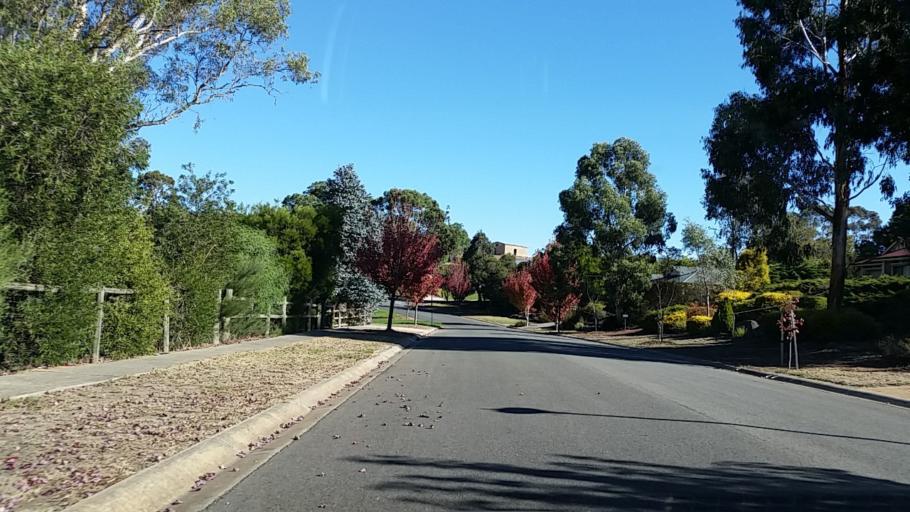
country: AU
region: South Australia
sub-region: Mount Barker
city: Mount Barker
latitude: -35.0646
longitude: 138.8887
